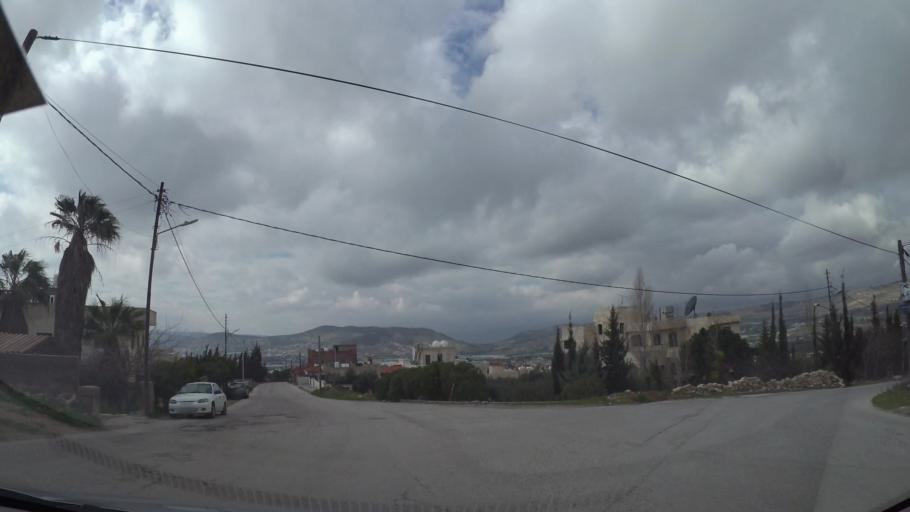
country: JO
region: Amman
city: Al Jubayhah
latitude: 32.0750
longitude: 35.8676
